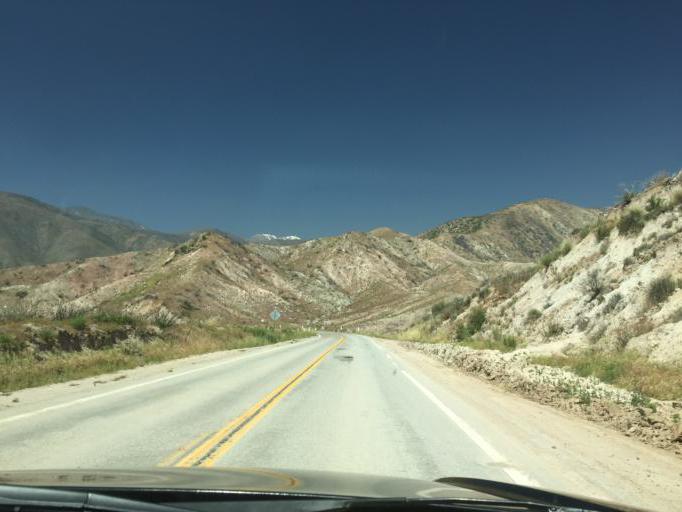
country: US
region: California
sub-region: San Bernardino County
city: Phelan
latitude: 34.3057
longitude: -117.5069
